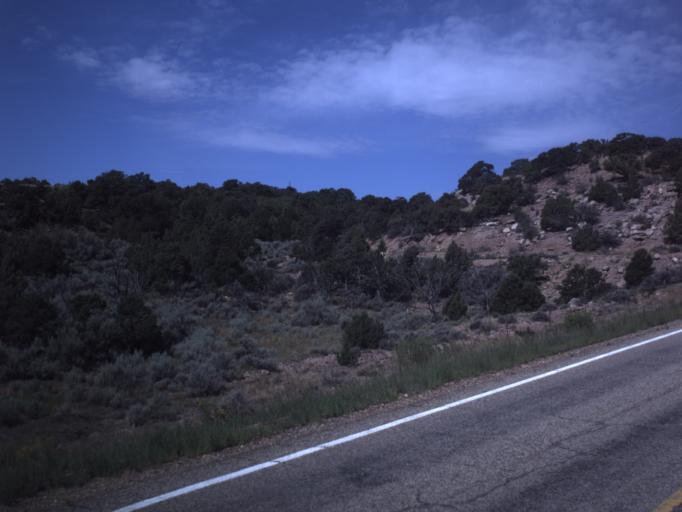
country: US
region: Utah
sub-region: Duchesne County
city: Duchesne
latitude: 40.3140
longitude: -110.3822
